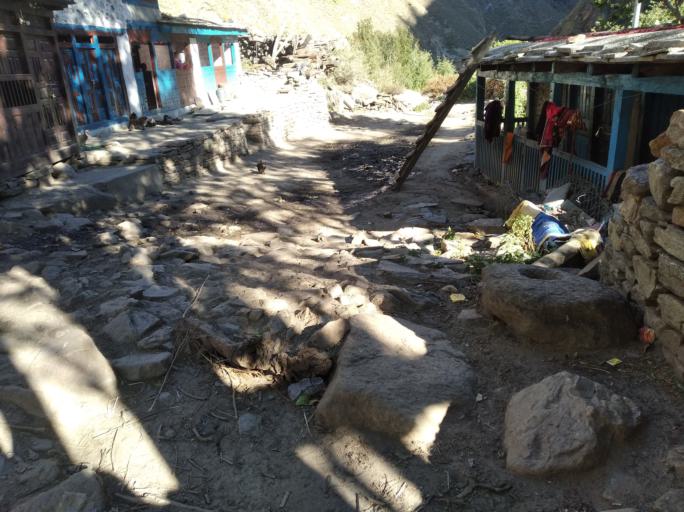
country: NP
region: Western Region
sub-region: Dhawalagiri Zone
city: Jomsom
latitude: 28.9375
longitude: 82.9556
